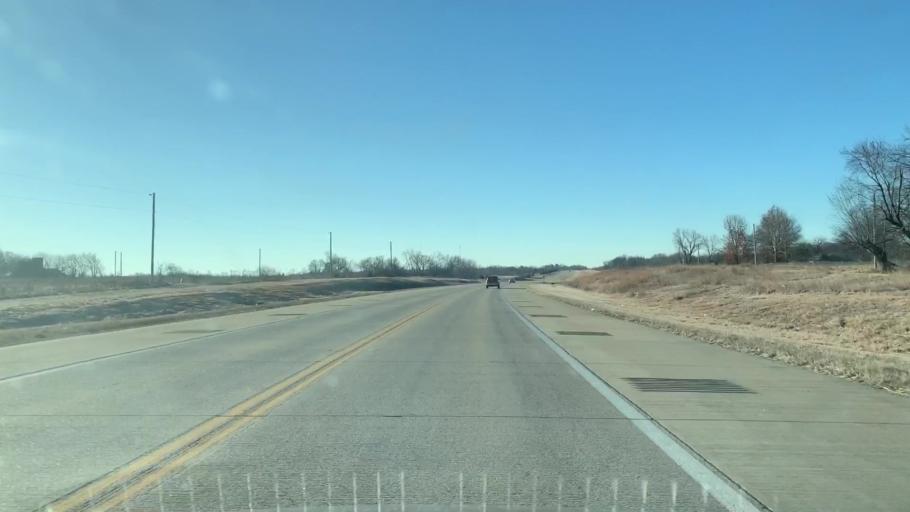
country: US
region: Kansas
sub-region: Crawford County
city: Arma
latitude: 37.5745
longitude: -94.7049
